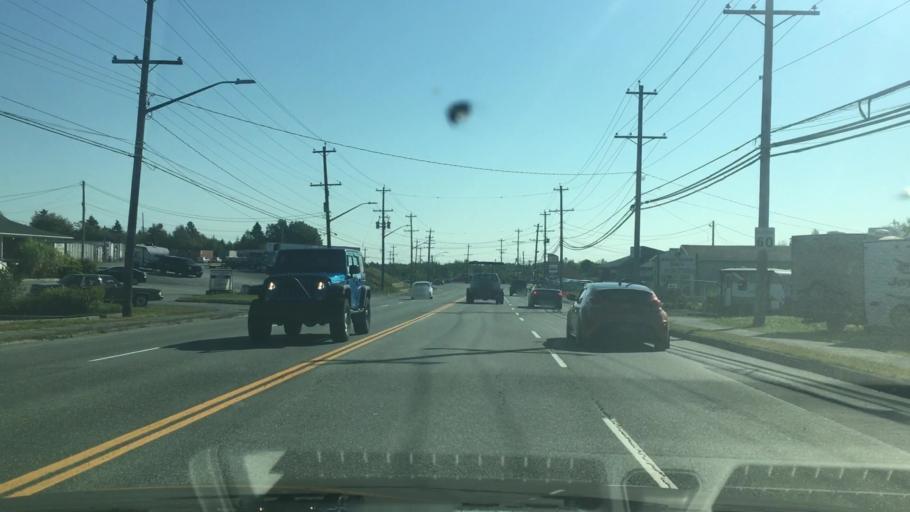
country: CA
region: Nova Scotia
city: Cole Harbour
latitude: 44.6983
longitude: -63.4899
